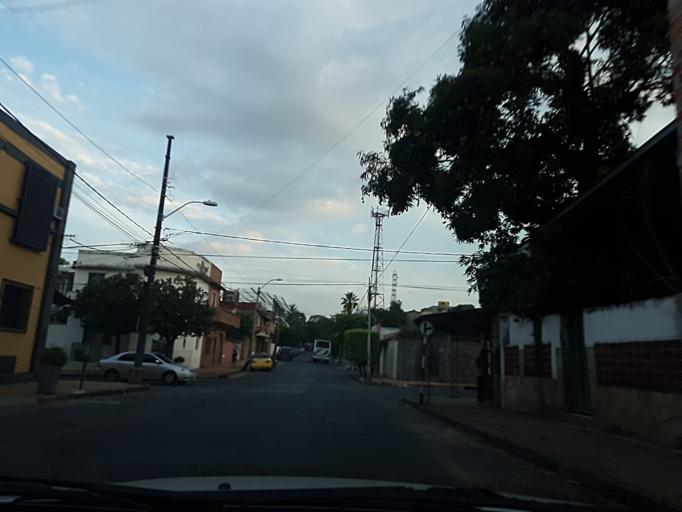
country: PY
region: Asuncion
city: Asuncion
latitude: -25.2946
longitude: -57.6218
